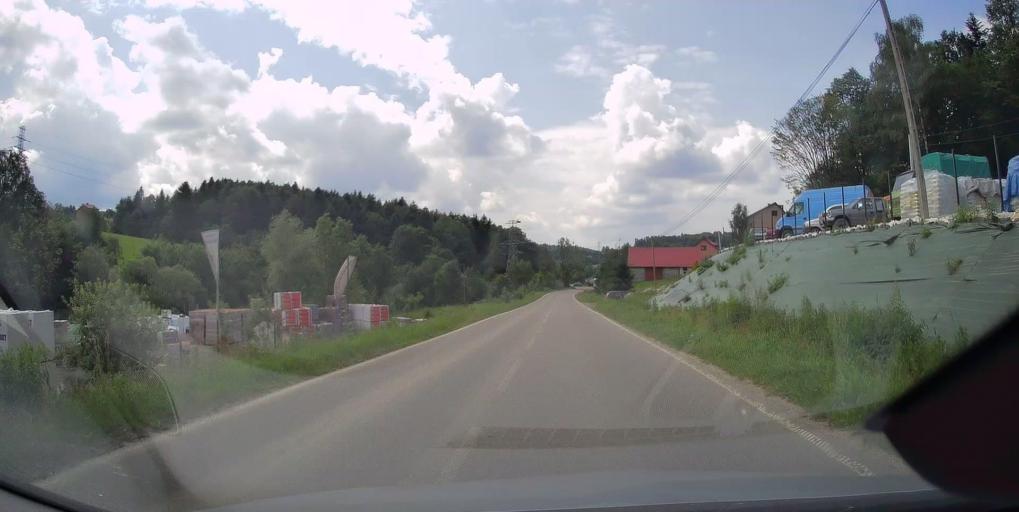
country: PL
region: Lesser Poland Voivodeship
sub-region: Powiat nowosadecki
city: Korzenna
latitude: 49.6710
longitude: 20.7760
